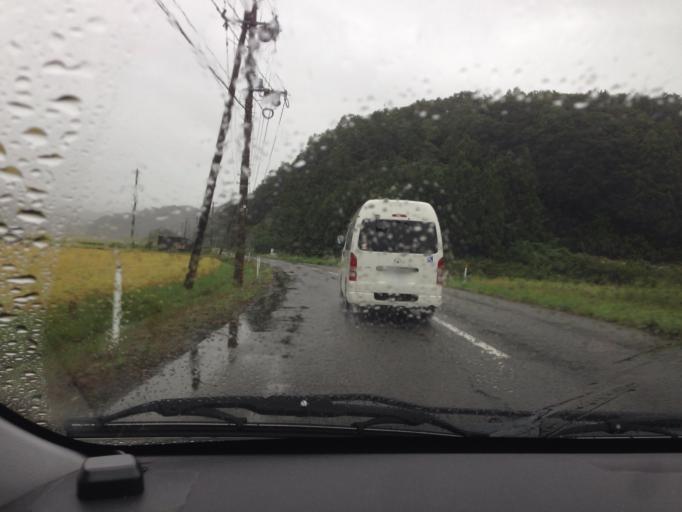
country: JP
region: Fukushima
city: Koriyama
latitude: 37.4194
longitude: 140.2761
